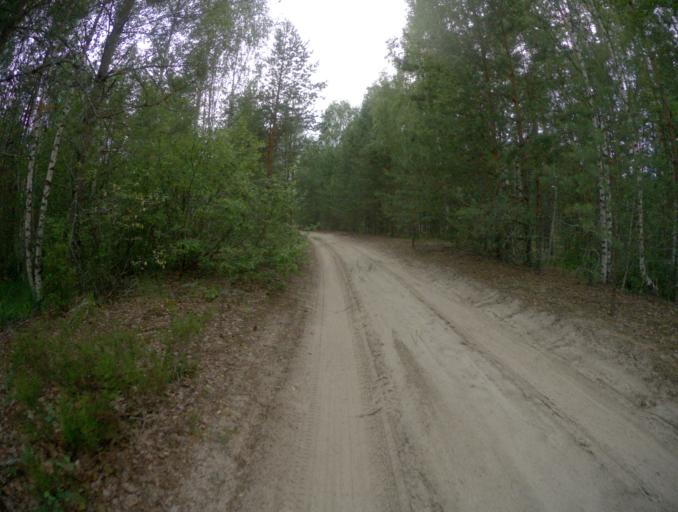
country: RU
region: Nizjnij Novgorod
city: Frolishchi
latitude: 56.4682
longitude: 42.6778
